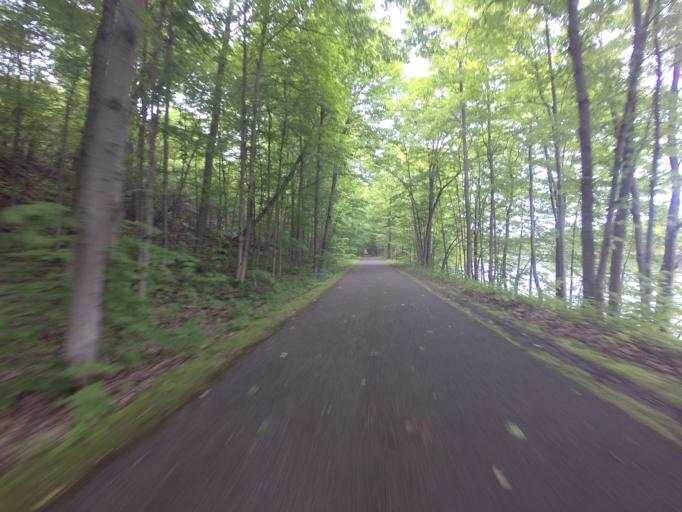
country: US
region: New York
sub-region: Jefferson County
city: Calcium
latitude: 43.9902
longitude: -75.8289
